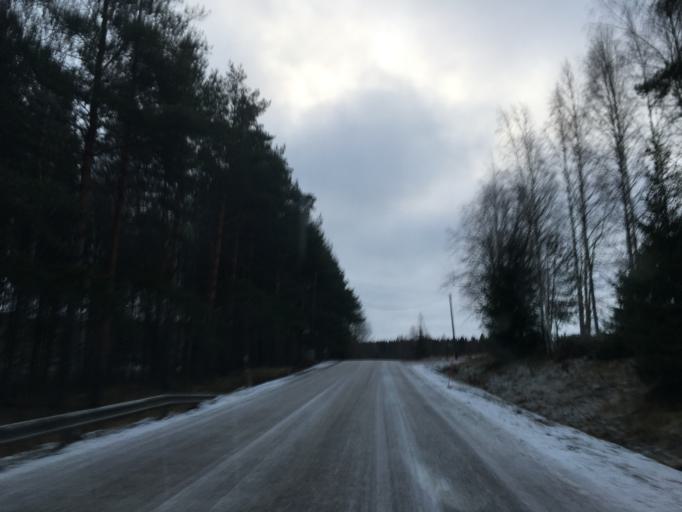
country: FI
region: Varsinais-Suomi
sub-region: Loimaa
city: Aura
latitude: 60.6070
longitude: 22.5661
